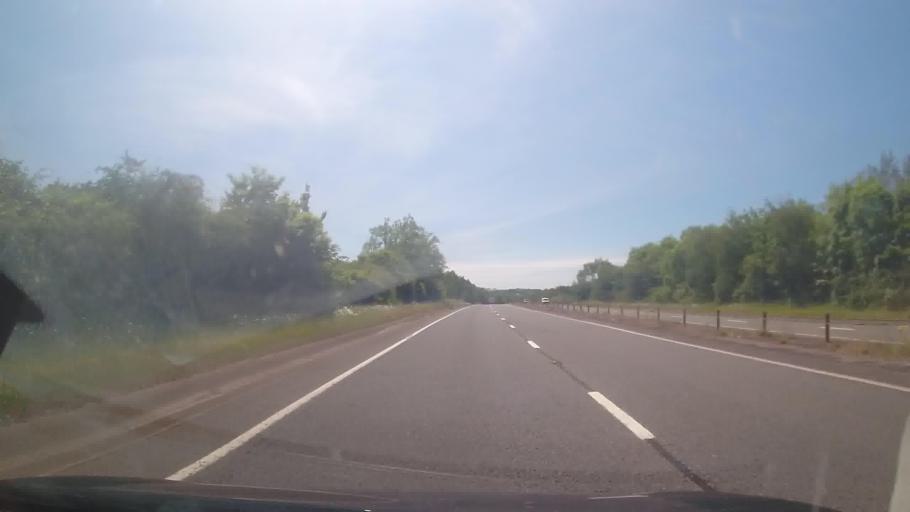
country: GB
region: England
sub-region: Devon
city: Ottery St Mary
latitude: 50.7830
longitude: -3.2466
